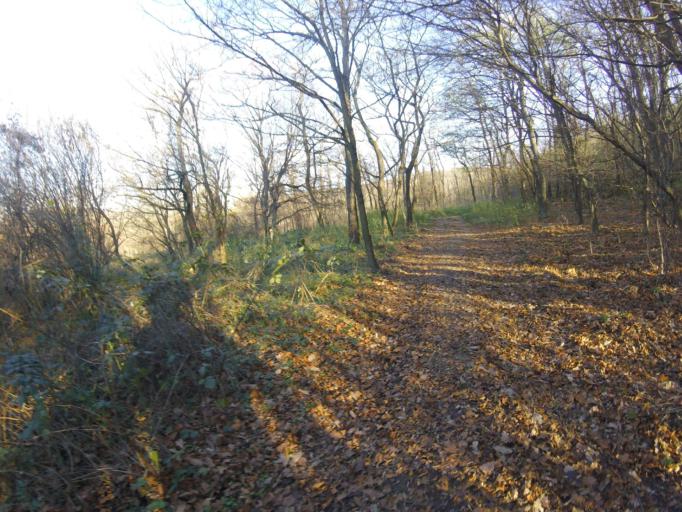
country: HU
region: Veszprem
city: Revfueloep
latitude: 46.9267
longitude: 17.5780
